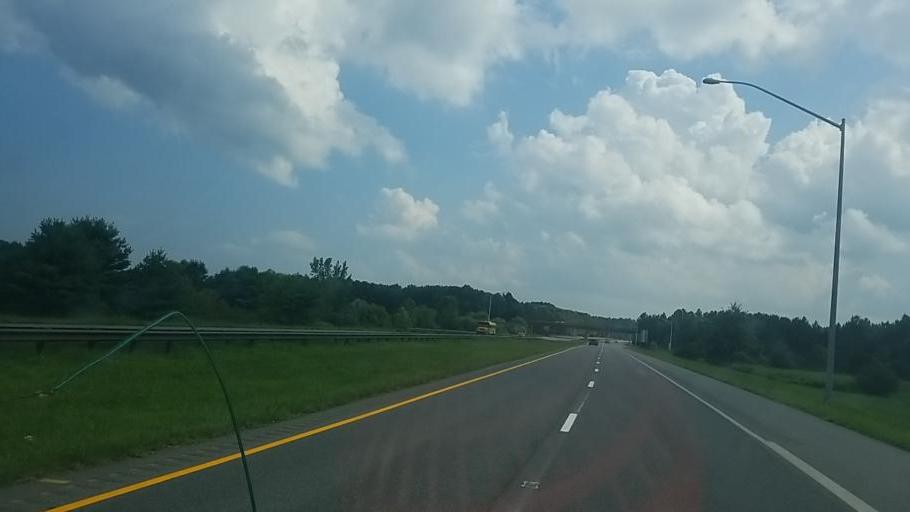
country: US
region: Maryland
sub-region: Worcester County
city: Ocean Pines
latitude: 38.3804
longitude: -75.2068
